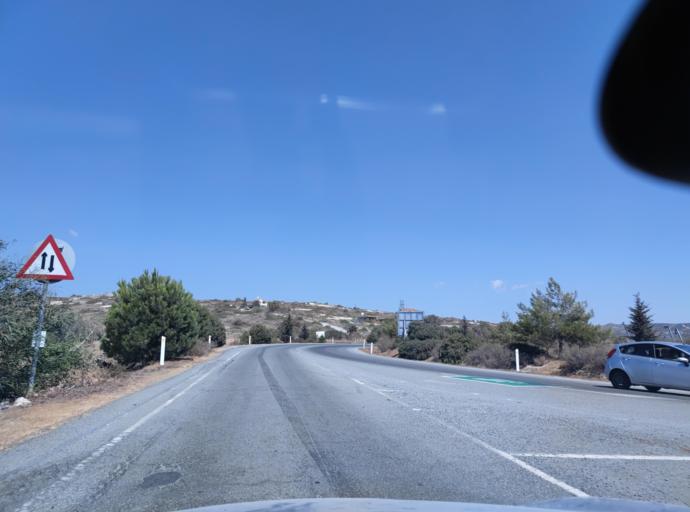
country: CY
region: Larnaka
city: Kofinou
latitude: 34.7561
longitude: 33.3161
